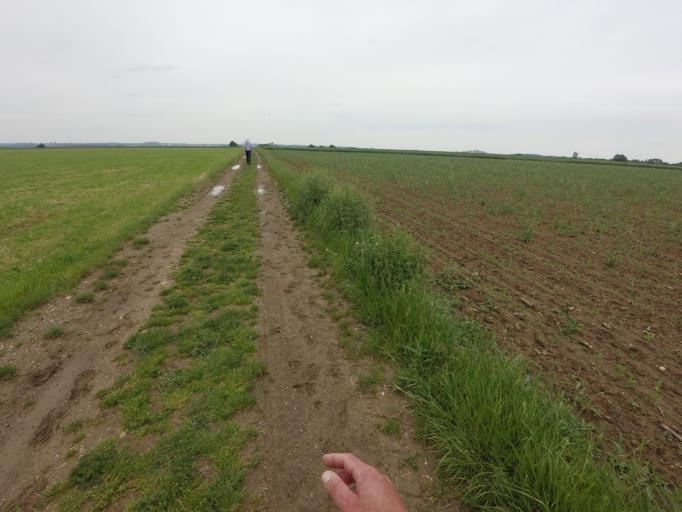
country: NL
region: Limburg
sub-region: Gemeente Voerendaal
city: Ubachsberg
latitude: 50.8654
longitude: 5.9511
